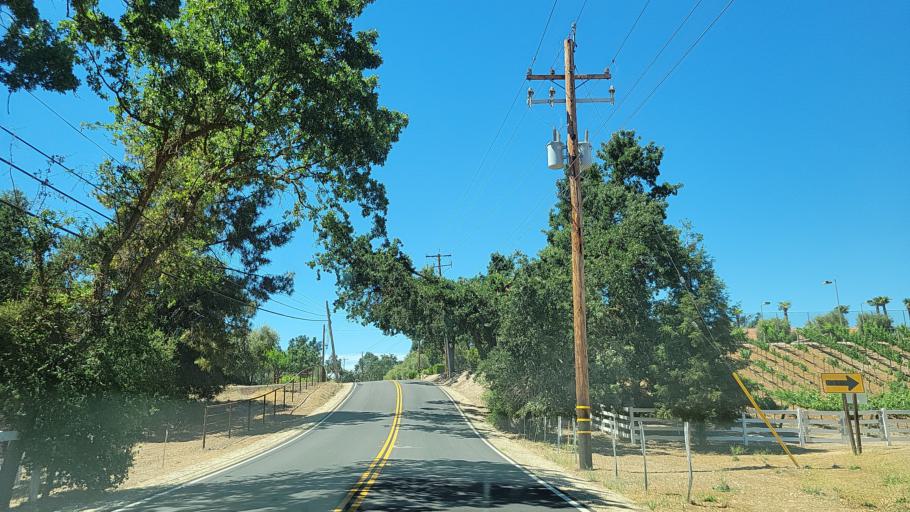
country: US
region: California
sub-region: San Luis Obispo County
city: Atascadero
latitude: 35.4996
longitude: -120.6480
